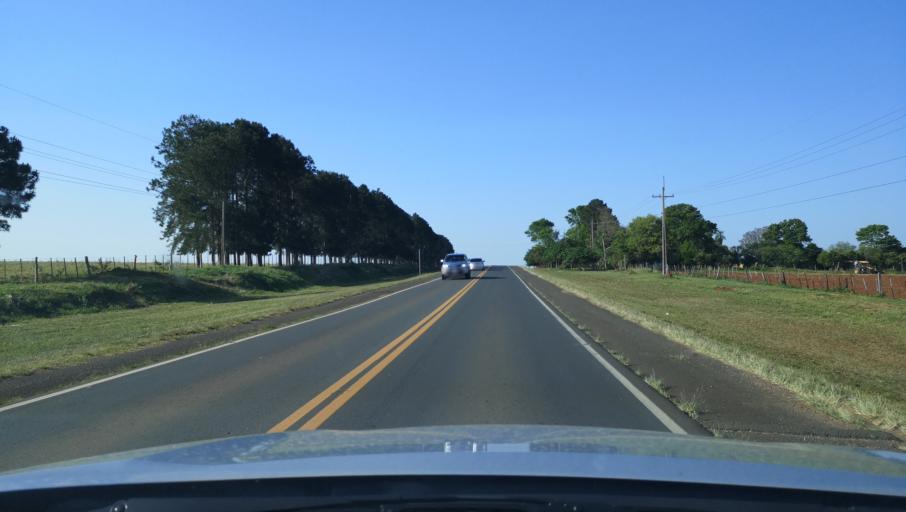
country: PY
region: Misiones
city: Santa Maria
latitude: -26.8426
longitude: -57.0370
